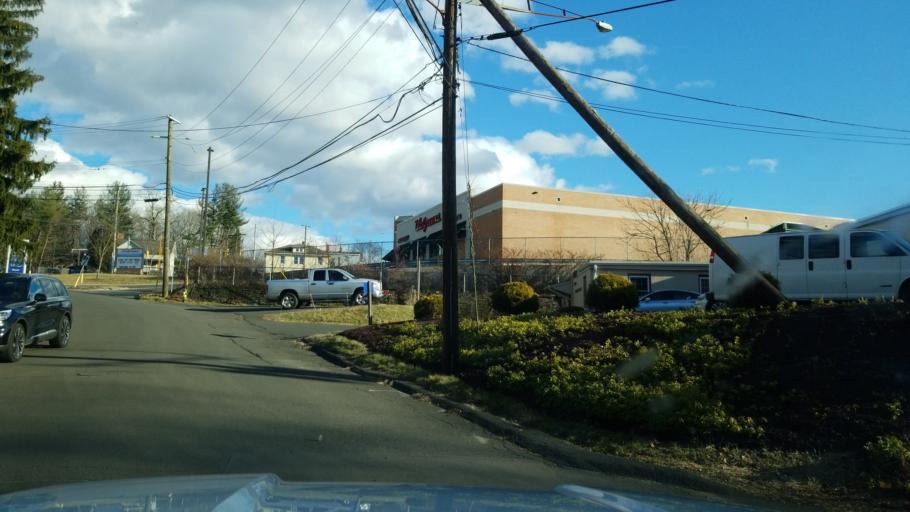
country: US
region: Connecticut
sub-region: Middlesex County
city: Middletown
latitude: 41.5484
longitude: -72.6405
